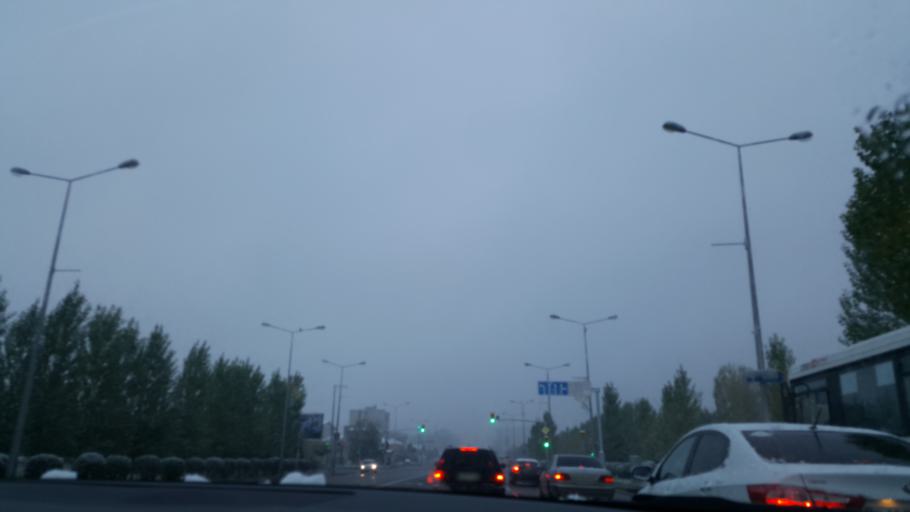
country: KZ
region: Astana Qalasy
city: Astana
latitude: 51.1454
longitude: 71.4972
